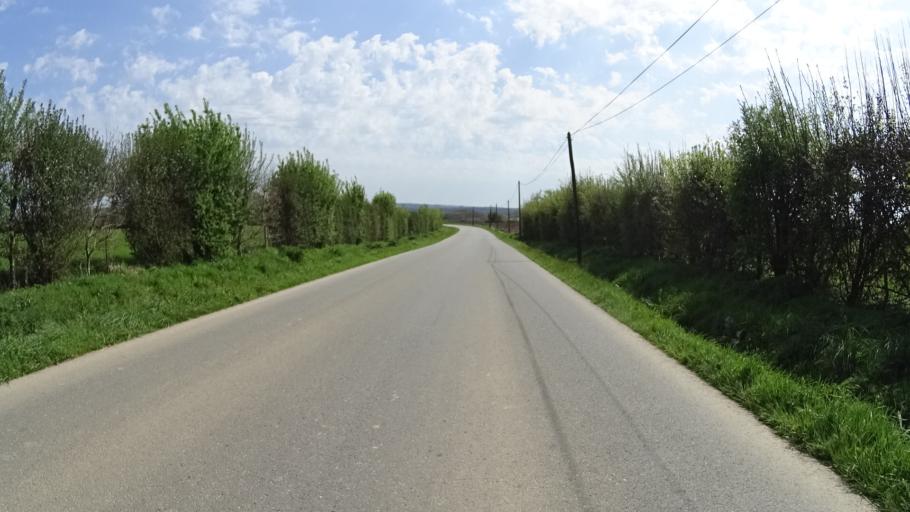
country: FR
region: Brittany
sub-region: Departement du Finistere
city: Sizun
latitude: 48.4329
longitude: -4.1166
